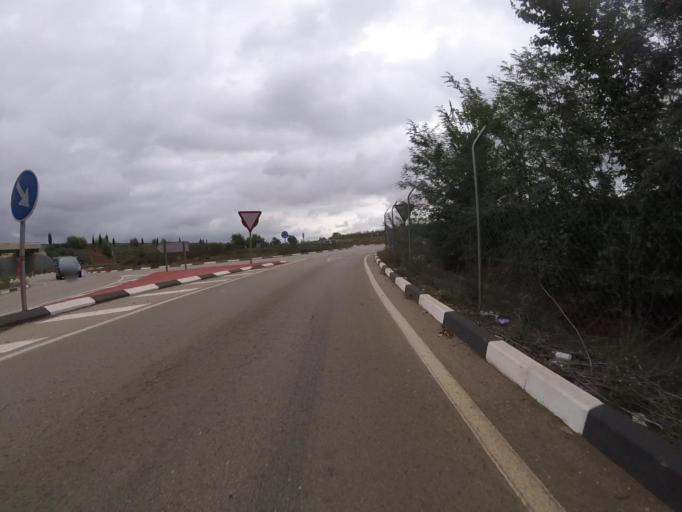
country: ES
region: Valencia
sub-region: Provincia de Castello
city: Cabanes
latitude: 40.1661
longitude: 0.0418
